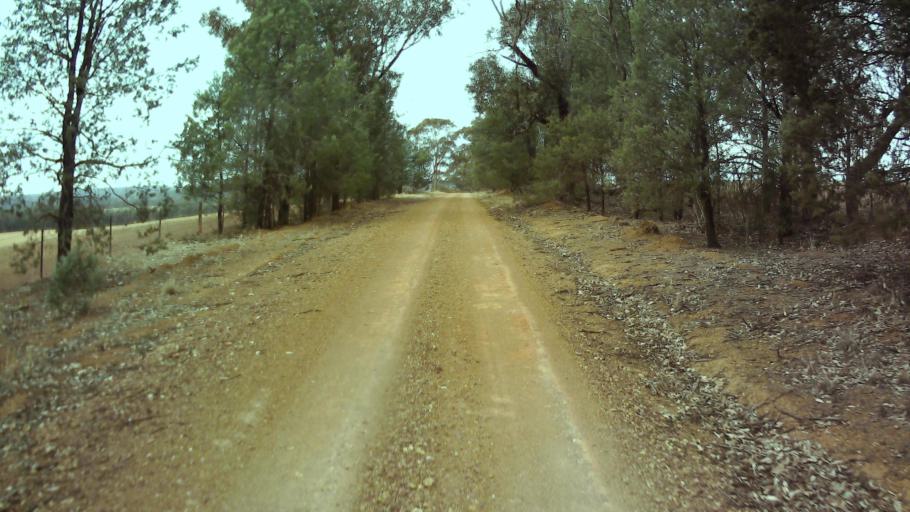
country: AU
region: New South Wales
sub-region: Weddin
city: Grenfell
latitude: -33.9274
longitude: 148.2525
